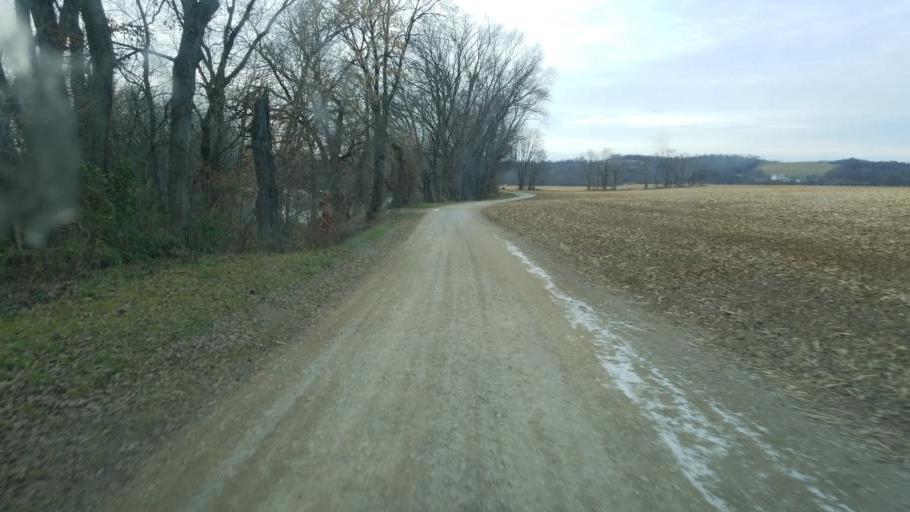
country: US
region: Ohio
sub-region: Muskingum County
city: Dresden
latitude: 40.1422
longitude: -81.9684
